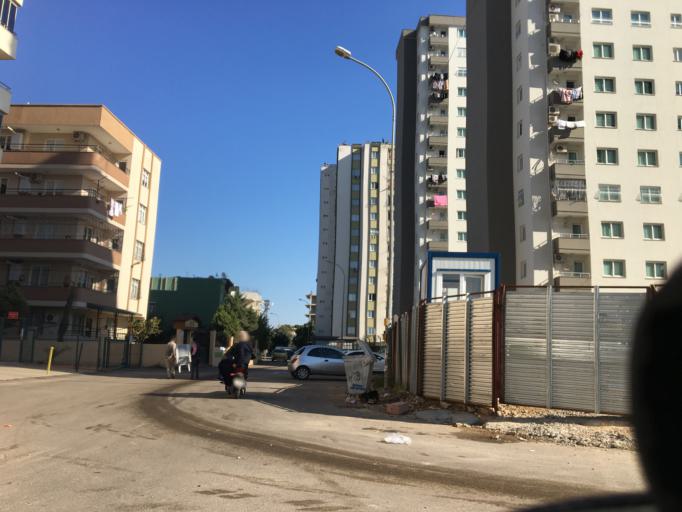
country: TR
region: Adana
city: Seyhan
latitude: 37.0118
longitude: 35.2901
